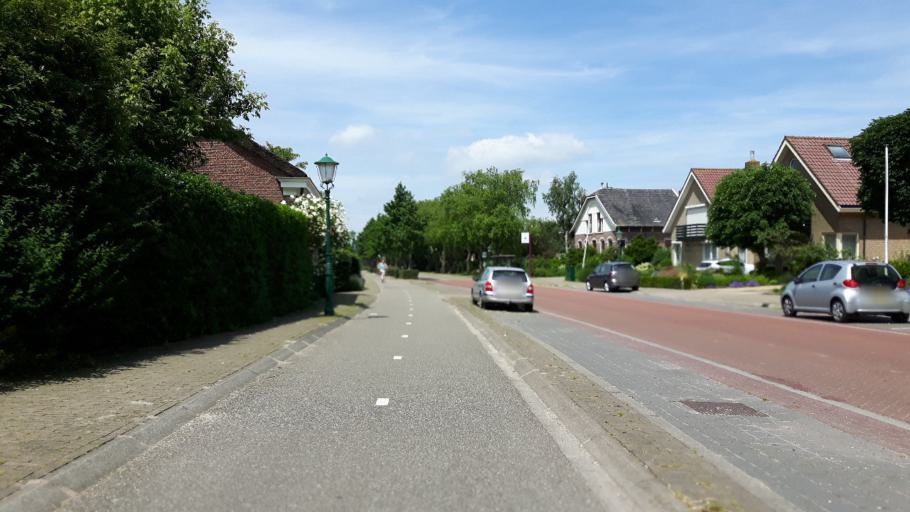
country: NL
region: Utrecht
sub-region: Gemeente Woerden
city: Woerden
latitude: 52.1114
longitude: 4.8425
